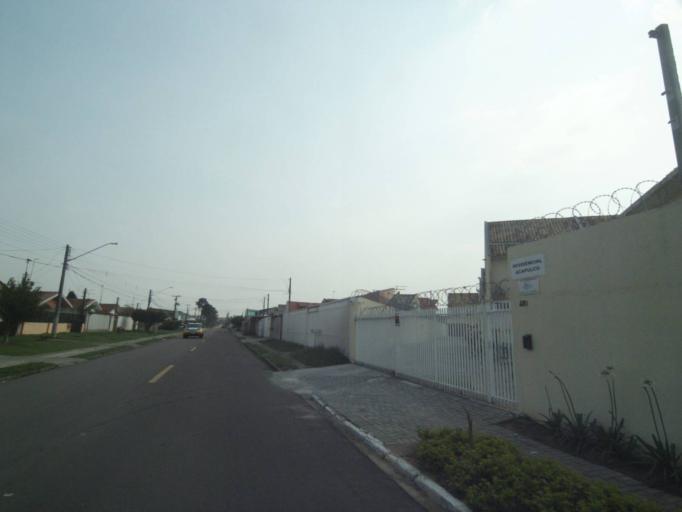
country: BR
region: Parana
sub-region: Sao Jose Dos Pinhais
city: Sao Jose dos Pinhais
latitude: -25.5274
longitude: -49.2288
